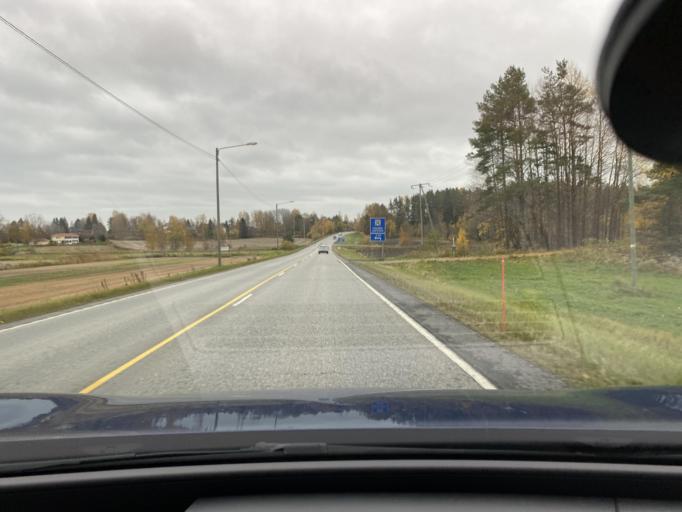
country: FI
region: Varsinais-Suomi
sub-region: Vakka-Suomi
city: Pyhaeranta
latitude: 60.9897
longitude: 21.5830
